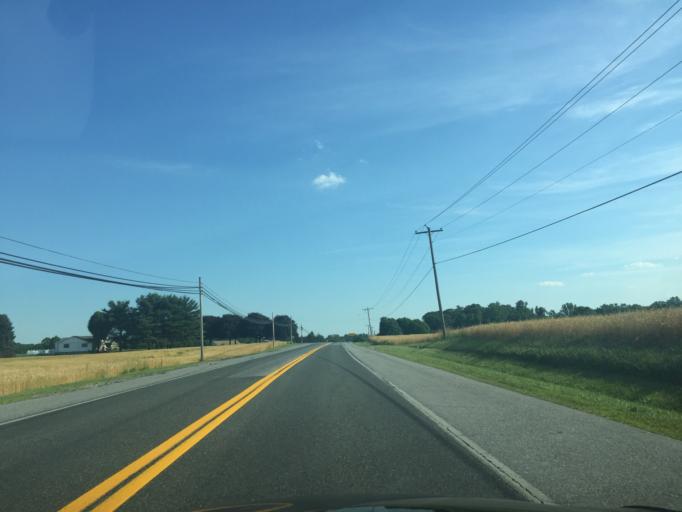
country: US
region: Maryland
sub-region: Harford County
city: Jarrettsville
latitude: 39.6184
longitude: -76.4765
